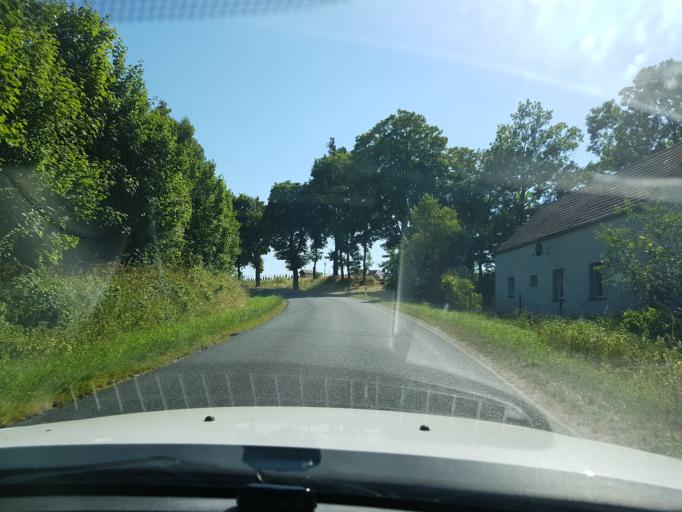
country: PL
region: West Pomeranian Voivodeship
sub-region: Powiat swidwinski
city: Slawoborze
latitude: 53.9115
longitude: 15.7742
